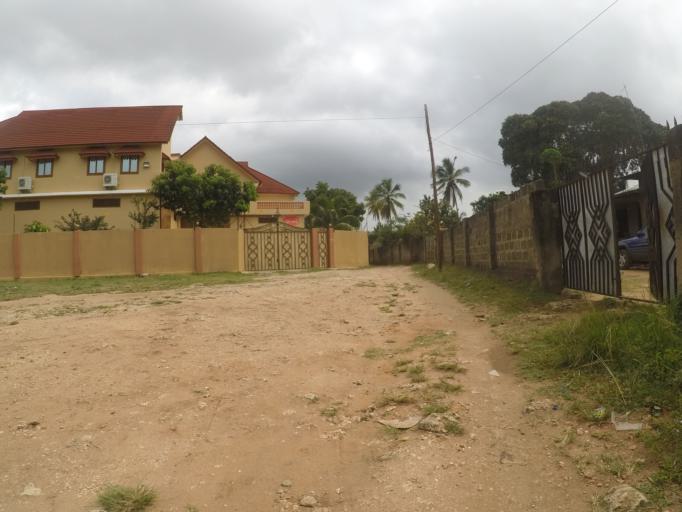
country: TZ
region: Zanzibar Urban/West
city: Zanzibar
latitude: -6.2133
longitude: 39.2201
